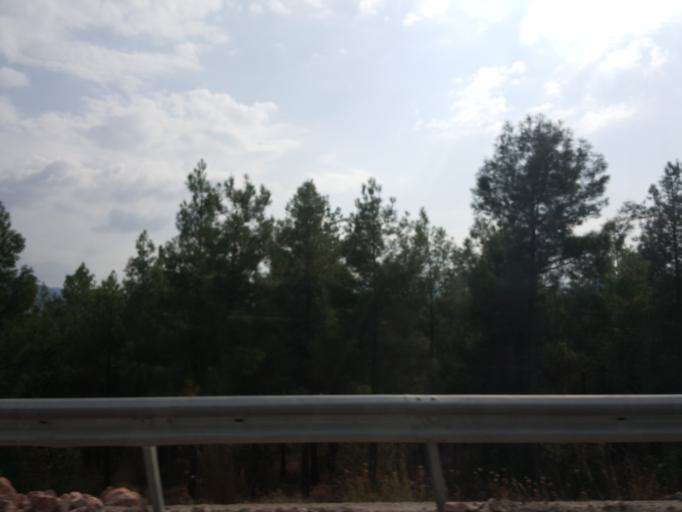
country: TR
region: Corum
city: Hacihamza
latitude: 41.1120
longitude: 34.3957
